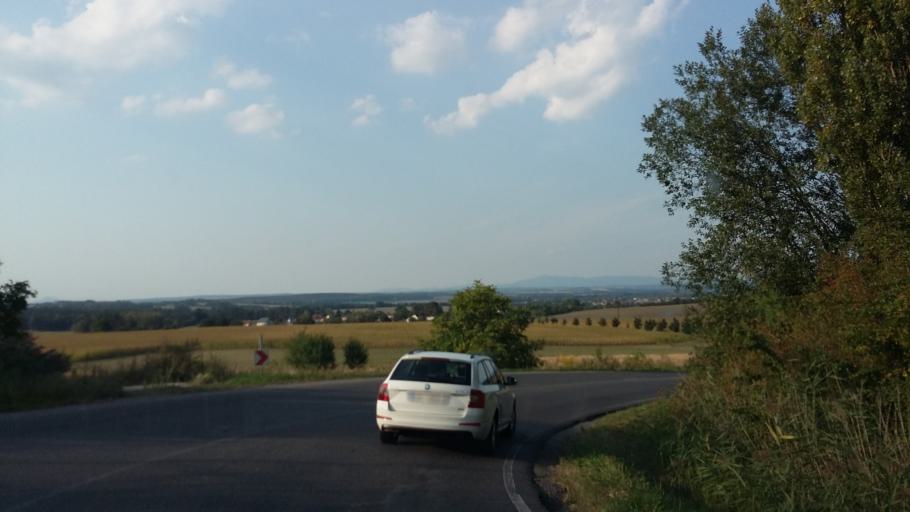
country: CZ
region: Central Bohemia
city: Kosmonosy
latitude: 50.4491
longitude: 14.9302
